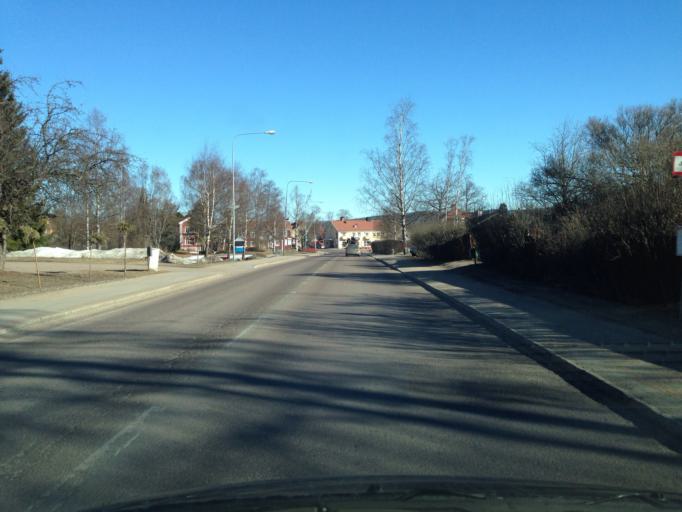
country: SE
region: Gaevleborg
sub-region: Ljusdals Kommun
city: Jaervsoe
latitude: 61.7117
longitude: 16.1671
